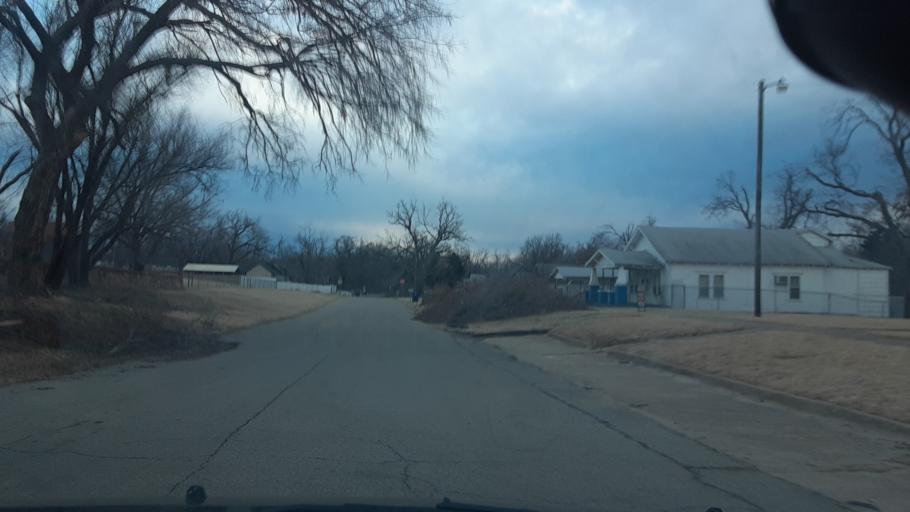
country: US
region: Oklahoma
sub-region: Logan County
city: Guthrie
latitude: 35.8738
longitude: -97.4228
